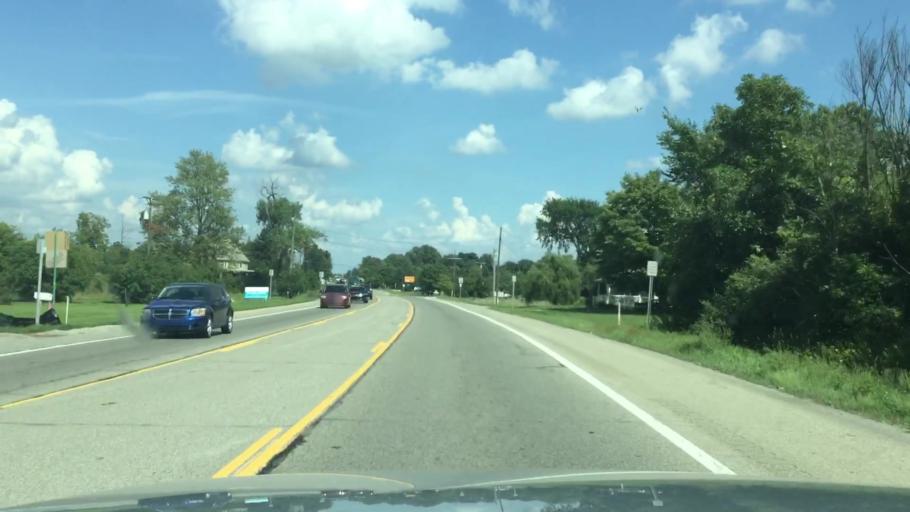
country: US
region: Michigan
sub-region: Washtenaw County
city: Ann Arbor
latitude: 42.2007
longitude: -83.6960
